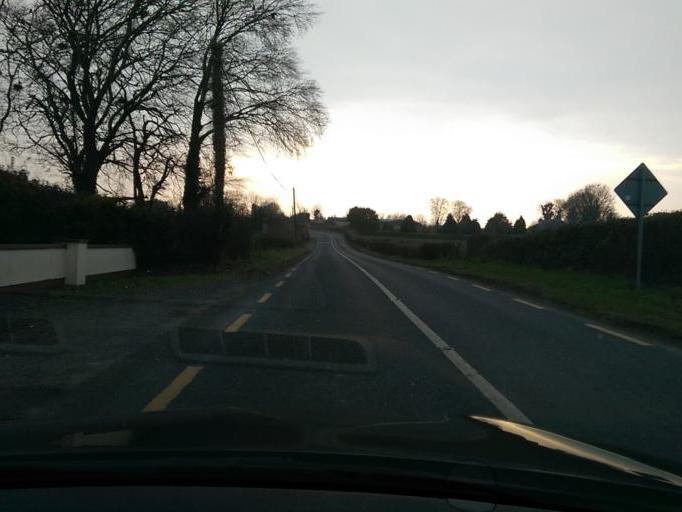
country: IE
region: Leinster
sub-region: An Longfort
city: Ballymahon
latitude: 53.5227
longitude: -7.8087
